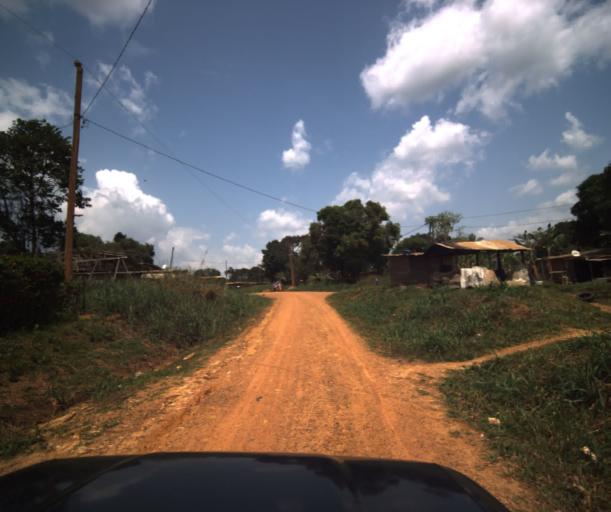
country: CM
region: Centre
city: Eseka
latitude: 3.5404
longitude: 11.0193
